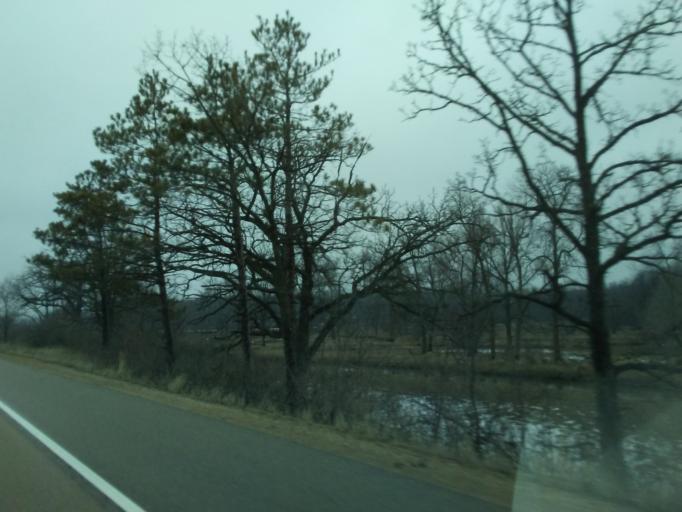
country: US
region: Wisconsin
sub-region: Dane County
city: Mazomanie
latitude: 43.1619
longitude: -89.8592
